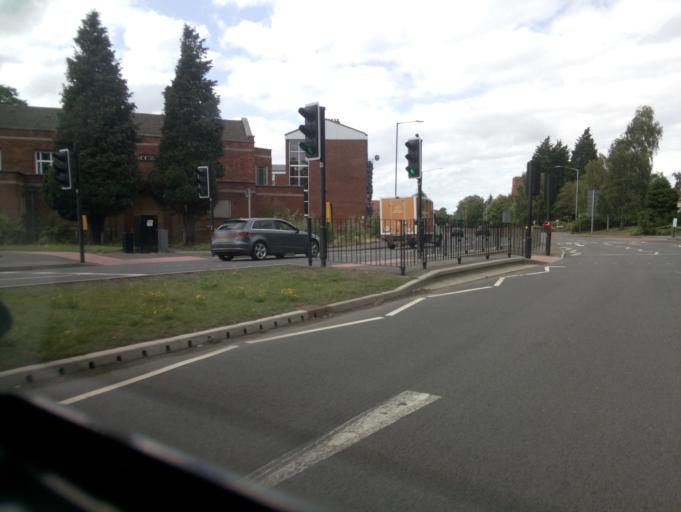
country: GB
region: England
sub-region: Warwickshire
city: Nuneaton
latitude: 52.5155
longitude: -1.4672
